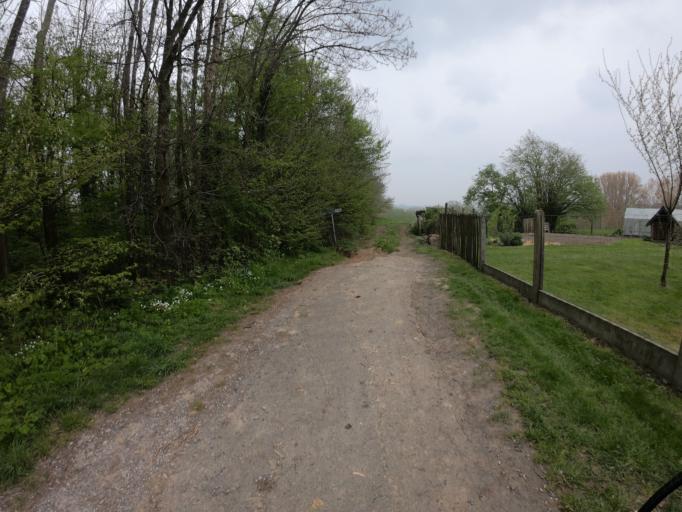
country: BE
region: Wallonia
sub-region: Province du Hainaut
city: Ellezelles
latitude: 50.7452
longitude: 3.6625
